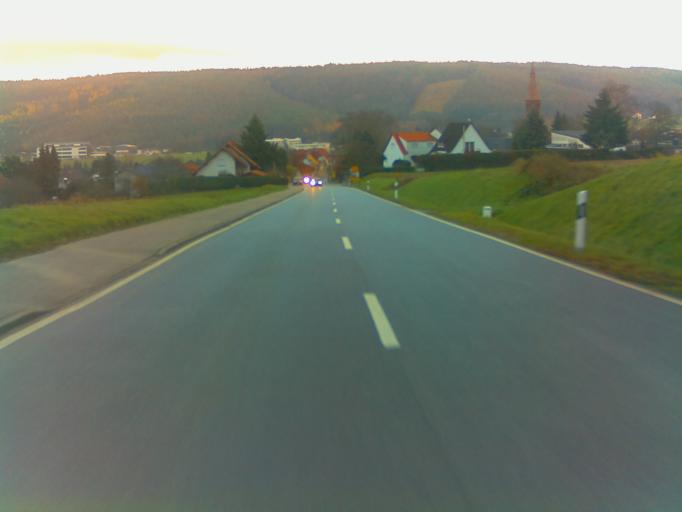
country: DE
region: Hesse
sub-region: Regierungsbezirk Darmstadt
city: Beerfelden
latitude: 49.5711
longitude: 8.9670
